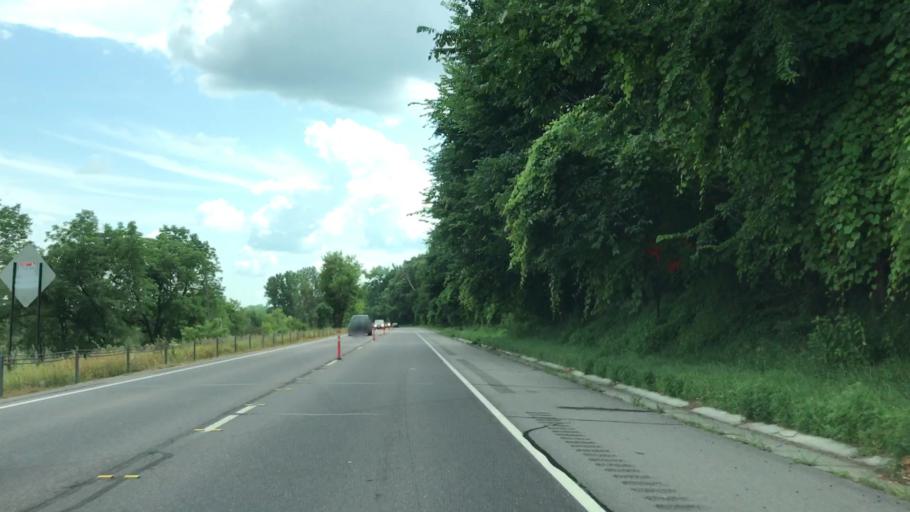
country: US
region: Minnesota
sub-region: Nicollet County
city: Saint Peter
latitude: 44.3790
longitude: -93.9691
